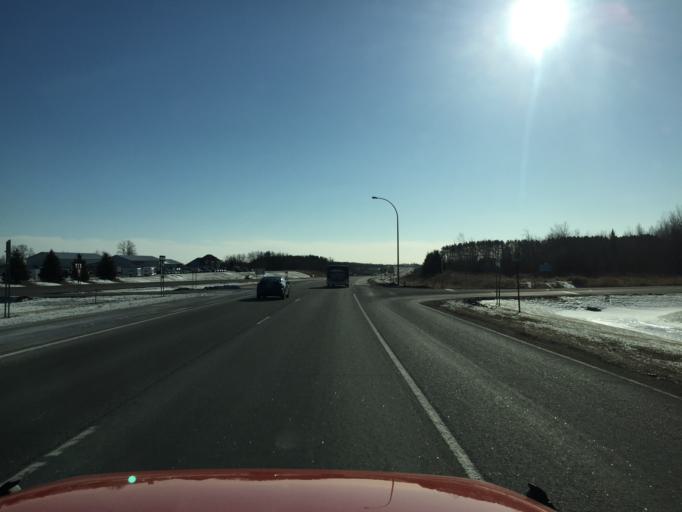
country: US
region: Minnesota
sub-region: Mille Lacs County
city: Milaca
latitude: 45.7850
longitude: -93.6514
